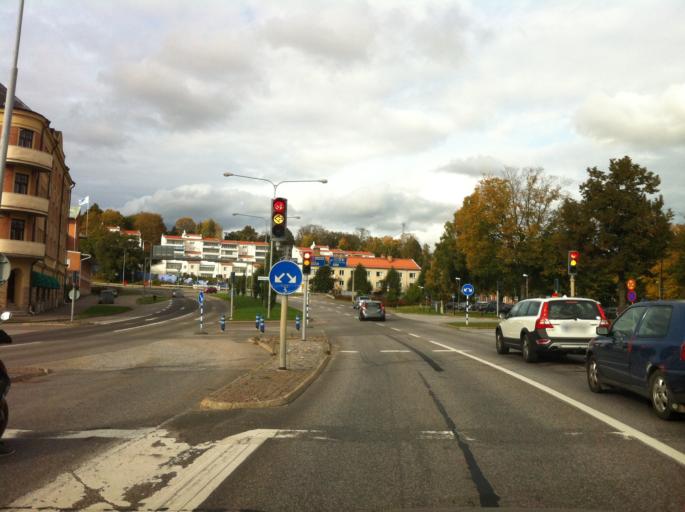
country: SE
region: OEstergoetland
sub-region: Motala Kommun
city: Motala
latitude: 58.5354
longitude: 15.0447
